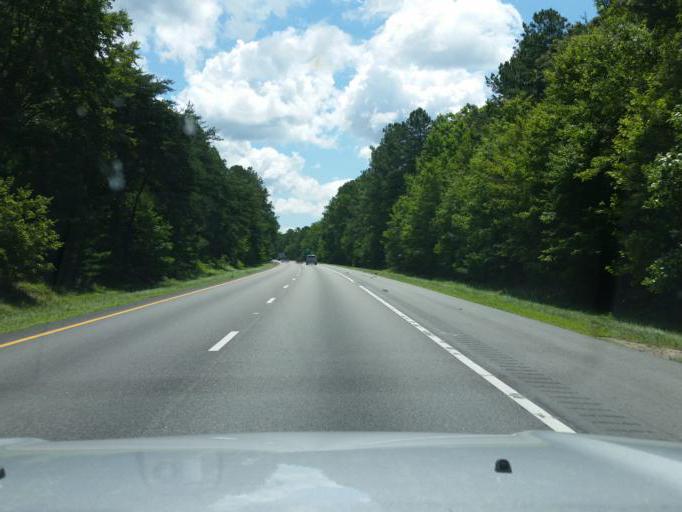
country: US
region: Virginia
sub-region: King William County
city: West Point
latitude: 37.4249
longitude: -76.8345
